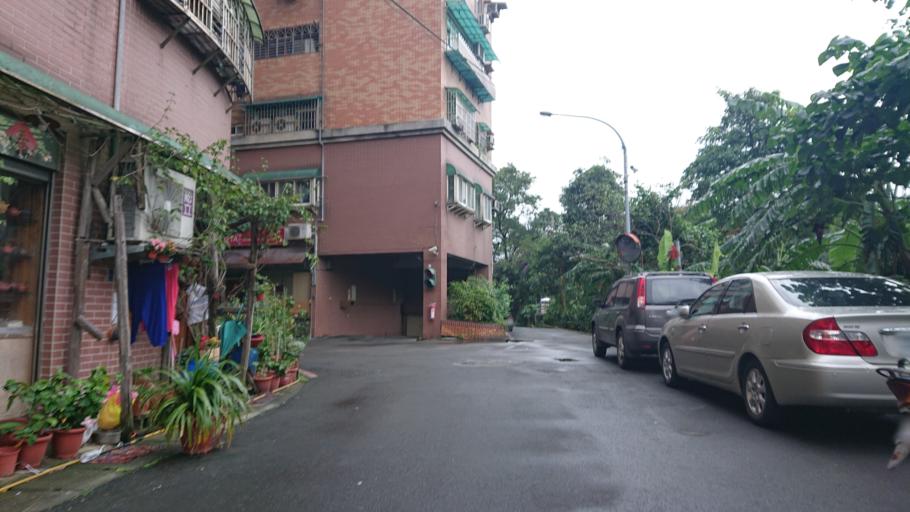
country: TW
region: Taiwan
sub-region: Taoyuan
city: Taoyuan
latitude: 24.9403
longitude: 121.3714
